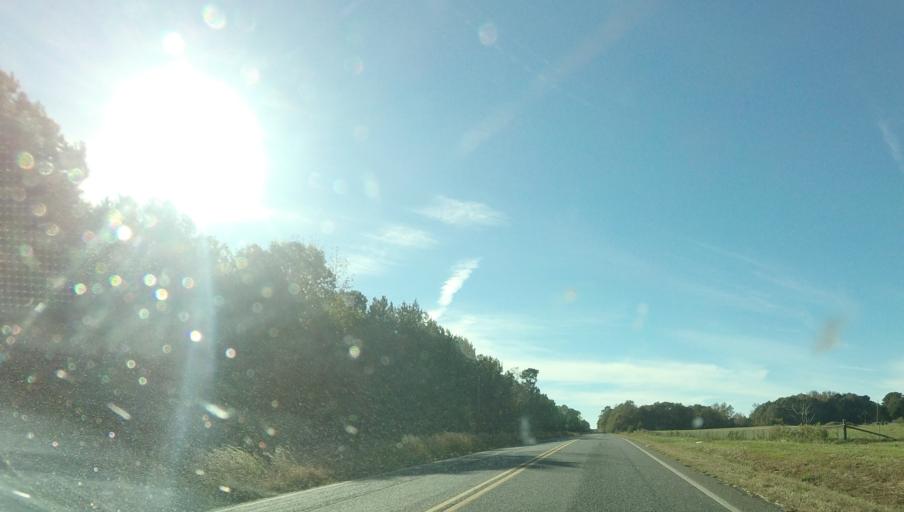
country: US
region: Georgia
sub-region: Talbot County
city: Talbotton
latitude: 32.6808
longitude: -84.5689
